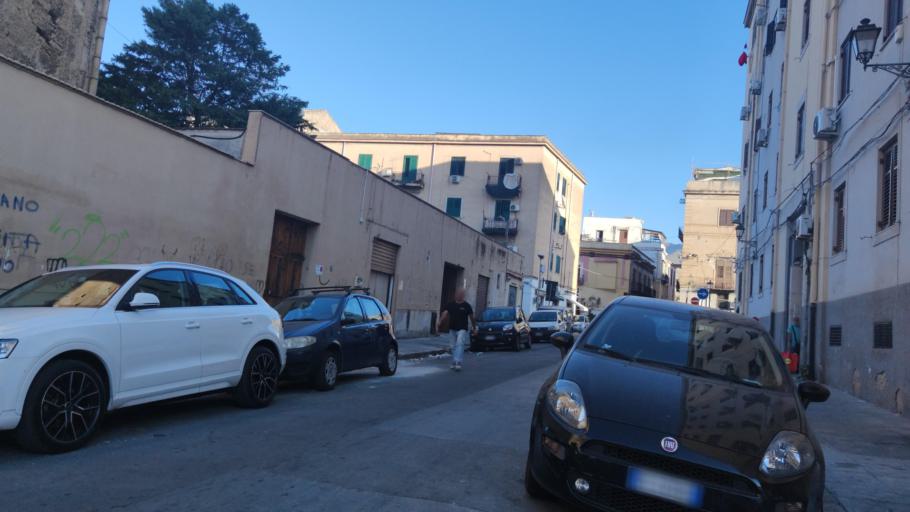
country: IT
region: Sicily
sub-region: Palermo
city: Palermo
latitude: 38.1109
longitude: 13.3611
